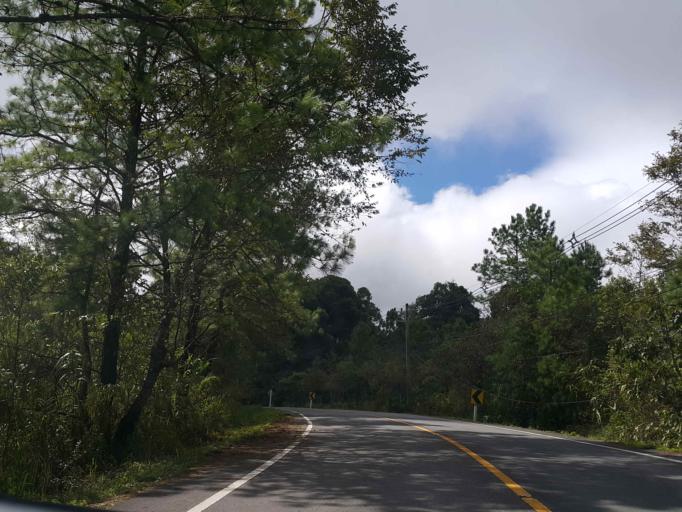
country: TH
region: Chiang Mai
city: Mae Chaem
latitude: 18.5362
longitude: 98.4933
